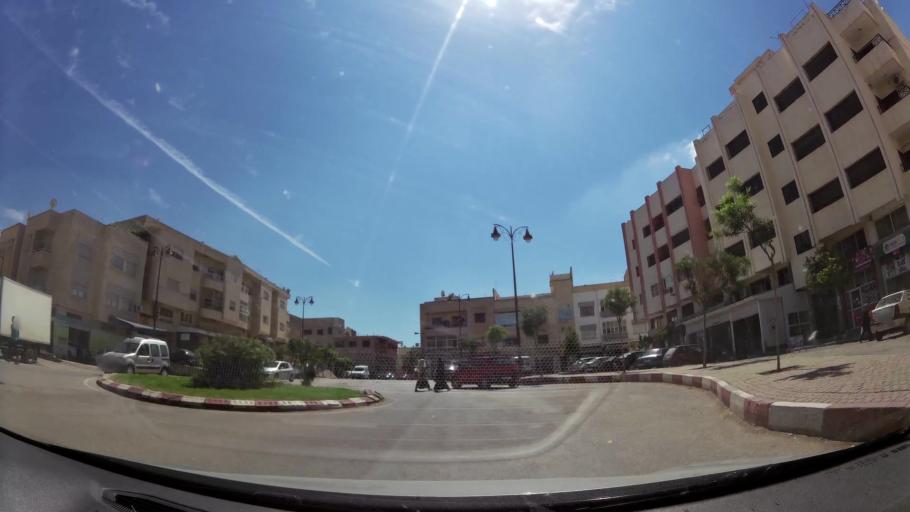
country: MA
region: Fes-Boulemane
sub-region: Fes
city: Fes
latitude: 34.0041
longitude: -4.9862
